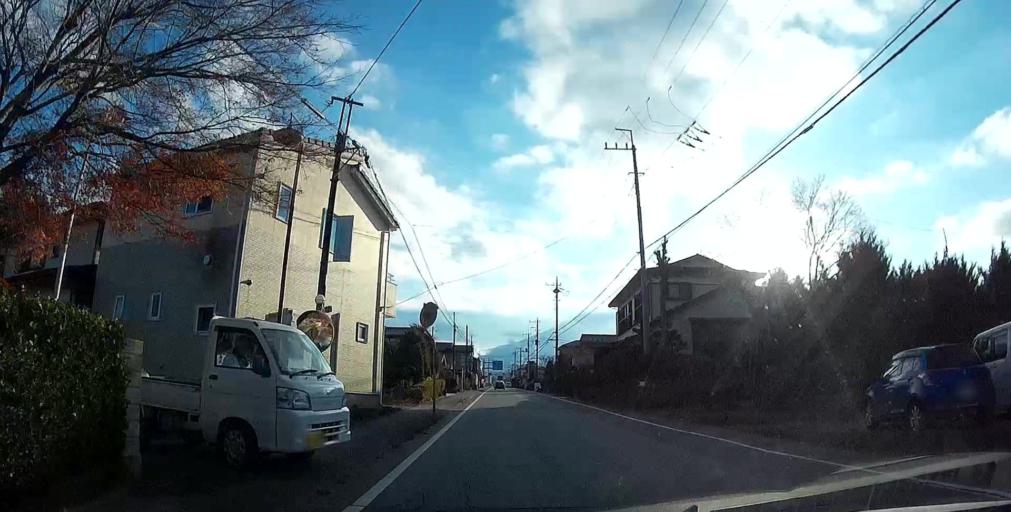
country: JP
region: Yamanashi
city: Fujikawaguchiko
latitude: 35.4801
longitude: 138.8171
